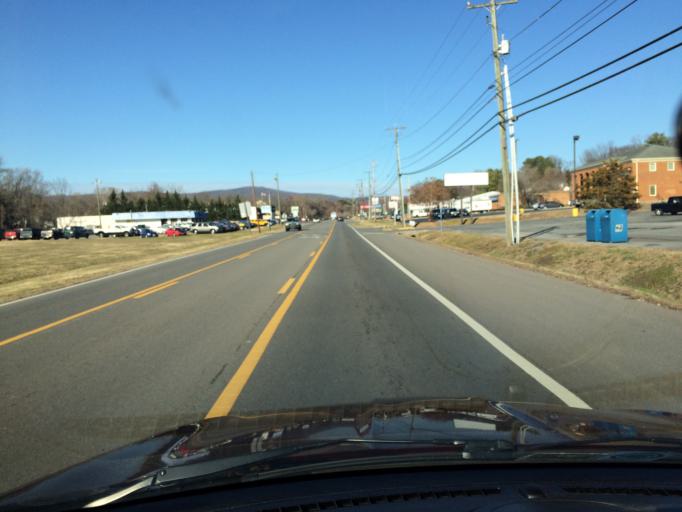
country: US
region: Virginia
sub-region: Roanoke County
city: Hollins
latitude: 37.3362
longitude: -79.9554
